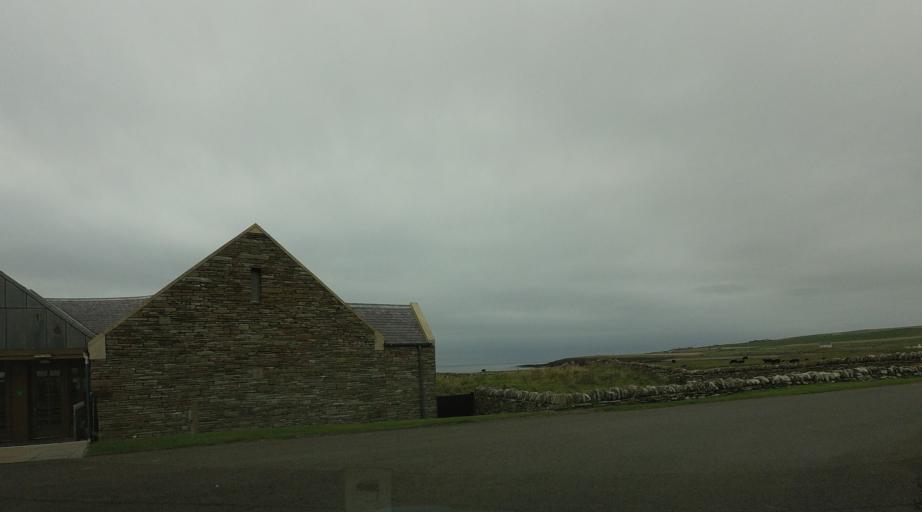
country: GB
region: Scotland
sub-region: Orkney Islands
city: Stromness
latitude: 59.0489
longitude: -3.3352
